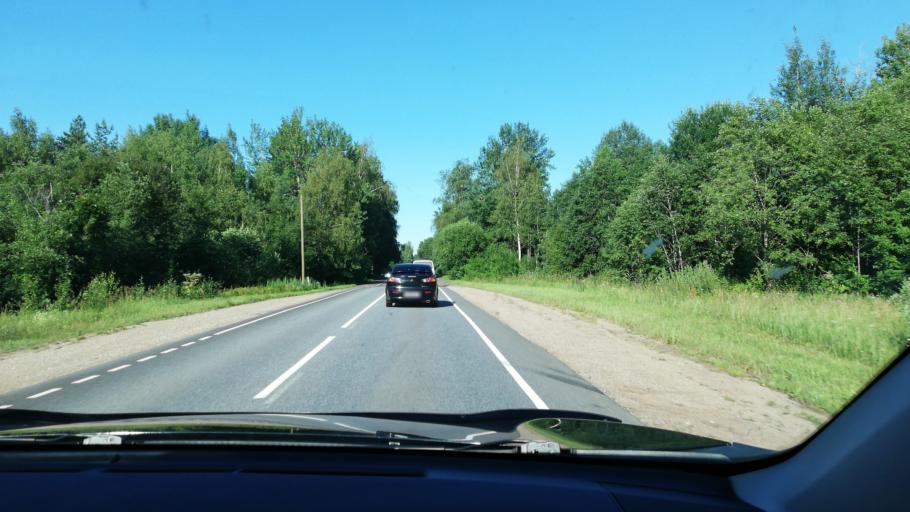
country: RU
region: Pskov
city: Nevel'
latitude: 56.0313
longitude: 30.1155
